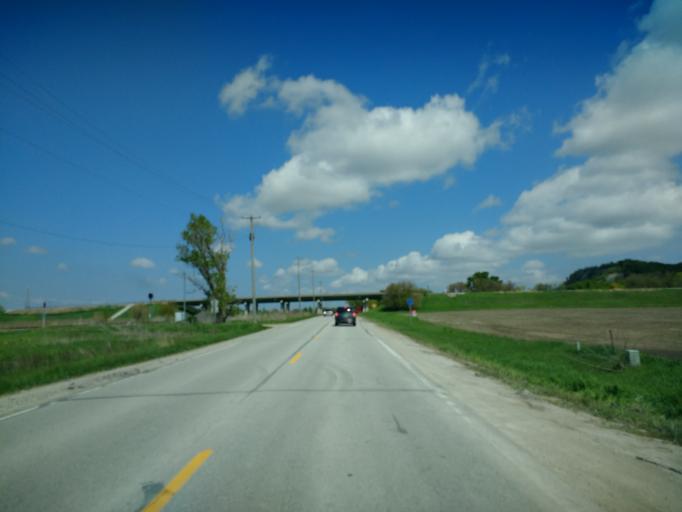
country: US
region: Iowa
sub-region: Harrison County
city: Missouri Valley
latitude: 41.4932
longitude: -95.8904
